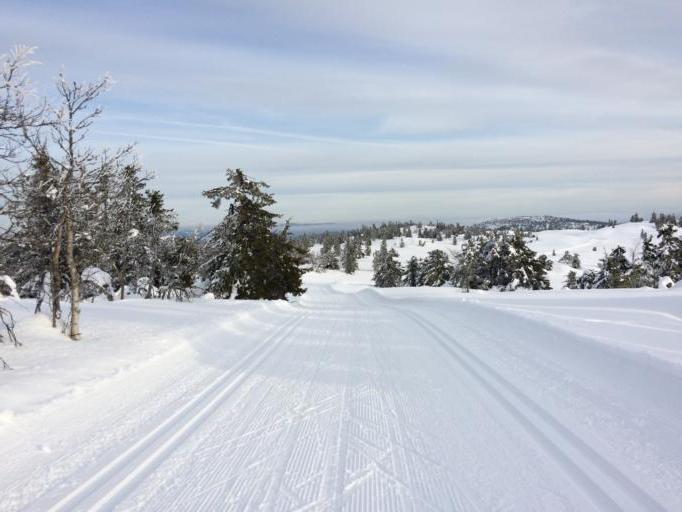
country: NO
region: Oppland
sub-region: Gausdal
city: Segalstad bru
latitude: 61.3273
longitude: 10.0356
